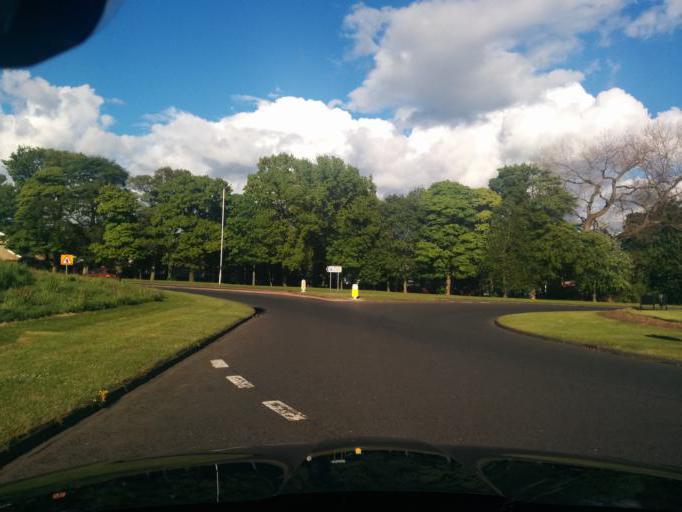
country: GB
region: England
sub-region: Northumberland
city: Cramlington
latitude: 55.0827
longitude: -1.5880
